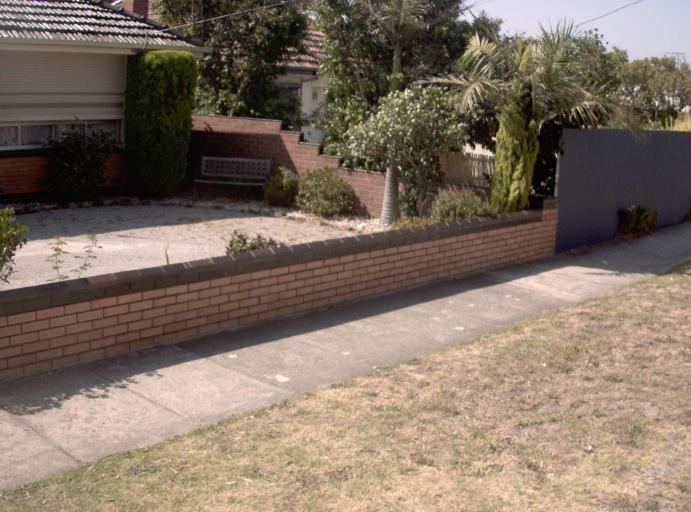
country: AU
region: Victoria
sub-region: Kingston
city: Mentone
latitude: -37.9704
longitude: 145.0737
